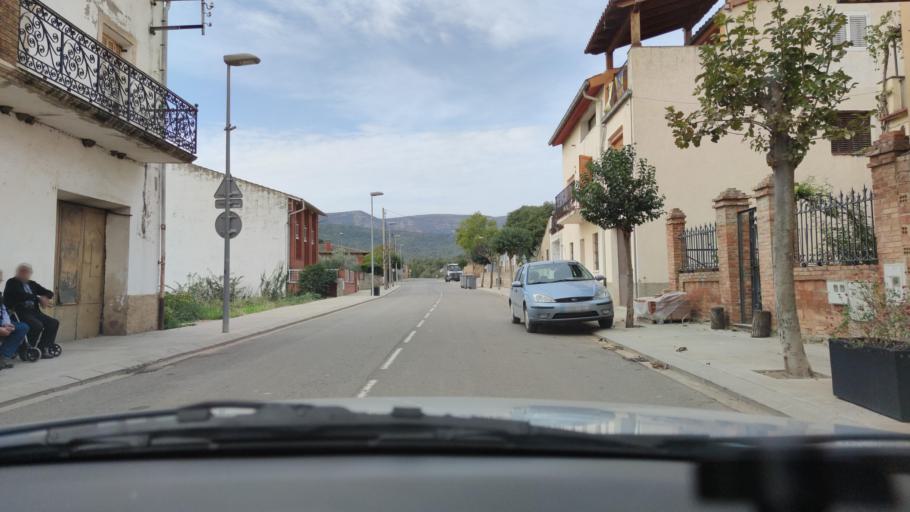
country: ES
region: Catalonia
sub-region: Provincia de Lleida
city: Artesa de Segre
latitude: 41.9938
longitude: 1.0206
